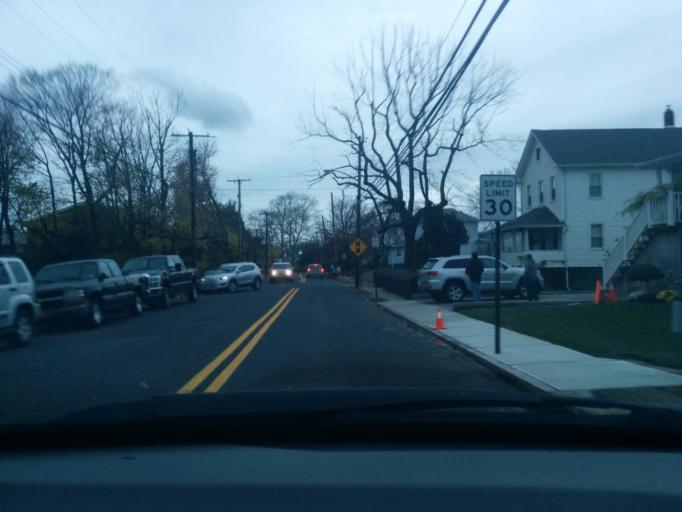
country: US
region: New Jersey
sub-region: Monmouth County
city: Monmouth Beach
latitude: 40.3202
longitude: -73.9837
